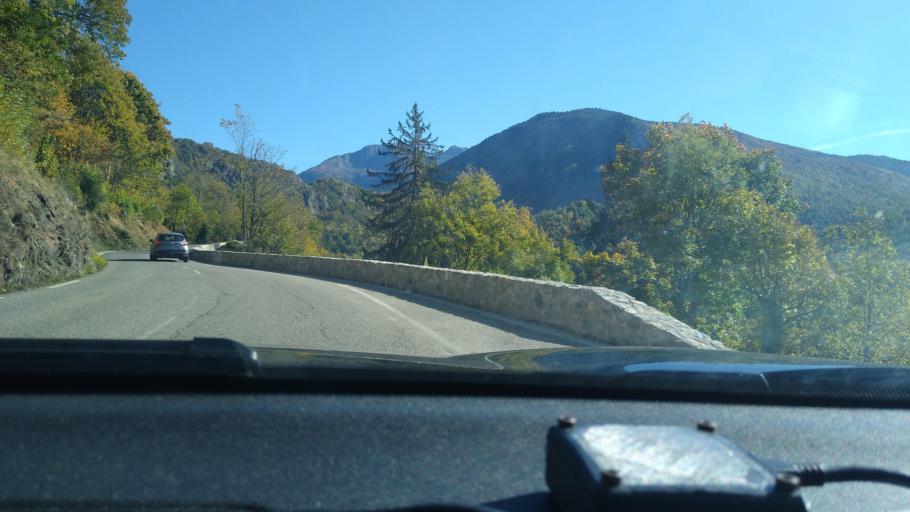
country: FR
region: Midi-Pyrenees
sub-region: Departement de l'Ariege
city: Ax-les-Thermes
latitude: 42.7235
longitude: 1.8403
